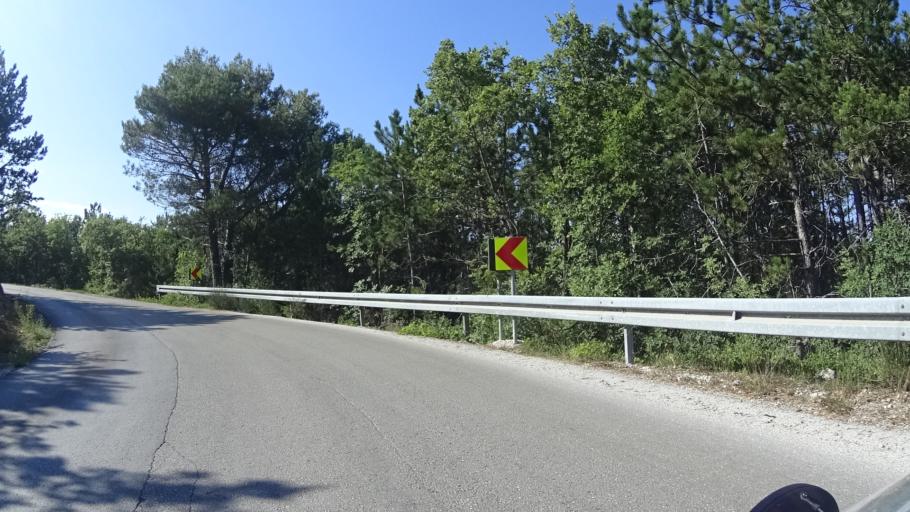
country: HR
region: Istarska
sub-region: Grad Labin
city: Labin
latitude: 45.0739
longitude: 14.1212
